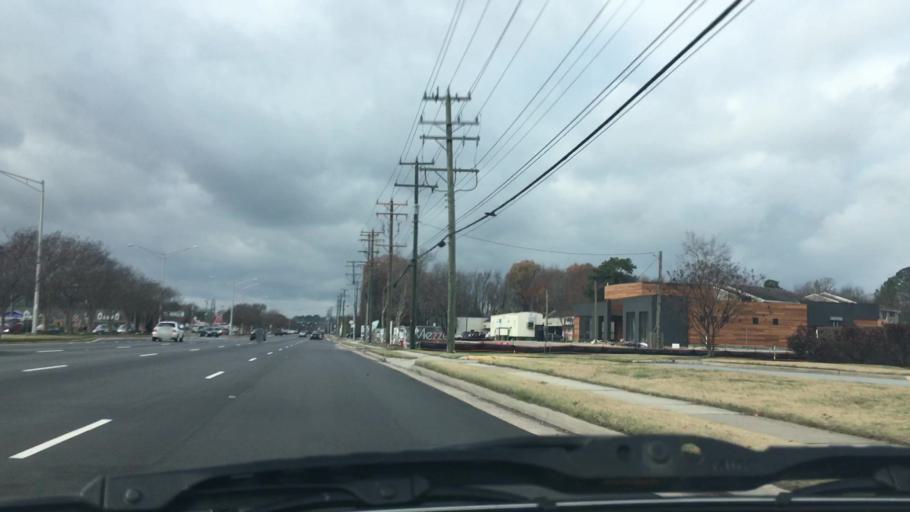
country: US
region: Virginia
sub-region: City of Chesapeake
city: Chesapeake
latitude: 36.8502
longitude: -76.1672
